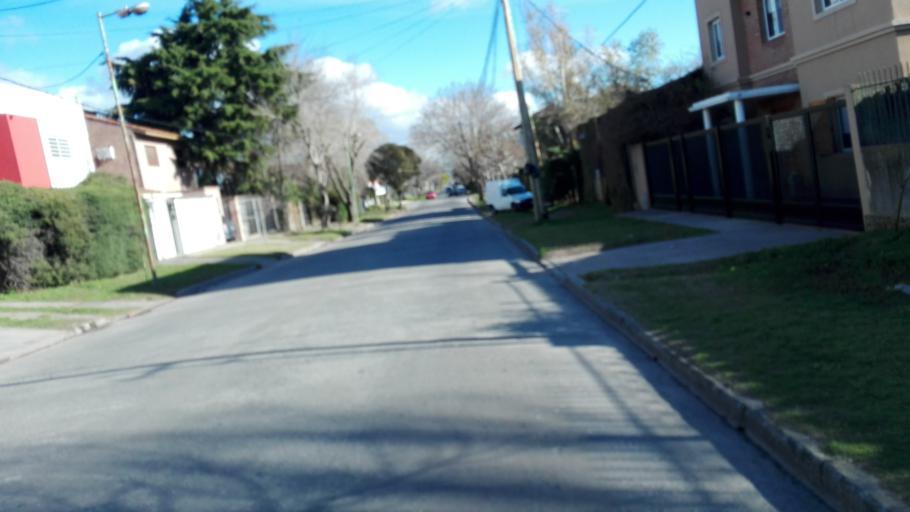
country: AR
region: Buenos Aires
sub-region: Partido de La Plata
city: La Plata
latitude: -34.8934
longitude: -58.0225
